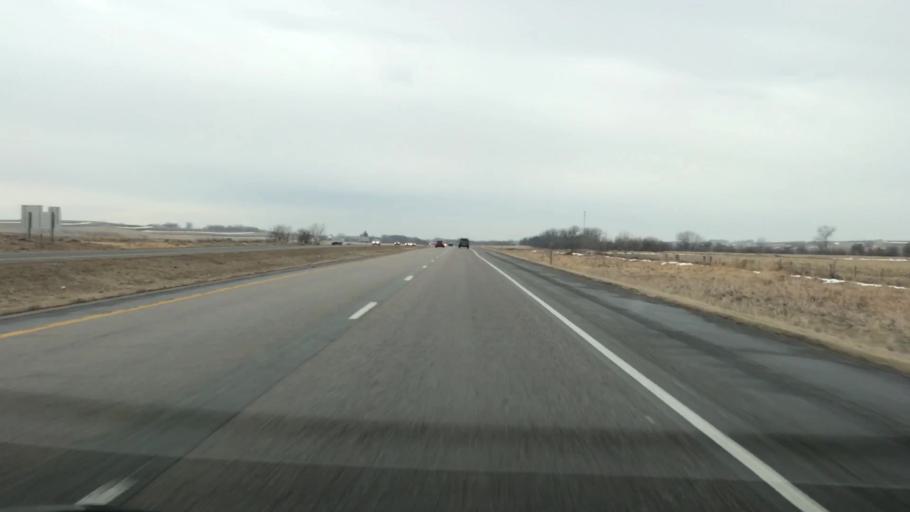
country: US
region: Iowa
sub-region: Pottawattamie County
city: Oakland
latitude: 41.4249
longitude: -95.6359
